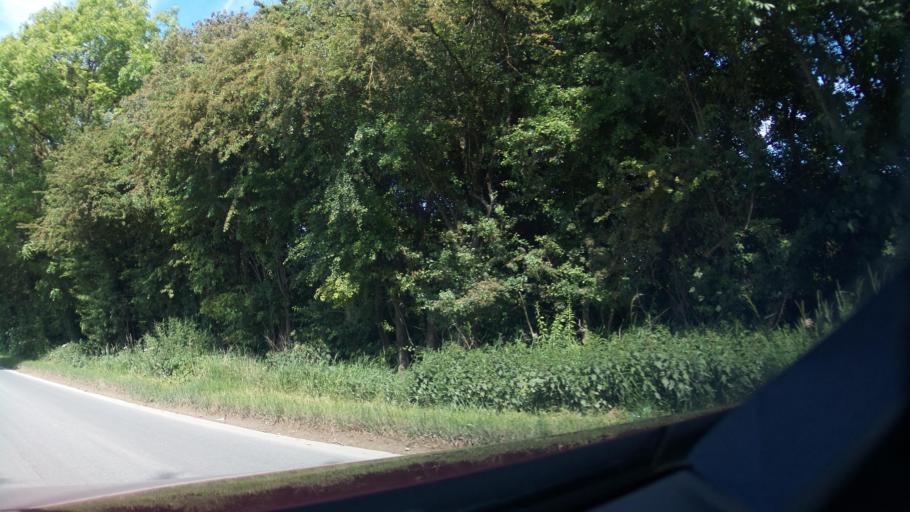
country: GB
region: England
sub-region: North Lincolnshire
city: Manton
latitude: 53.5005
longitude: -0.5736
